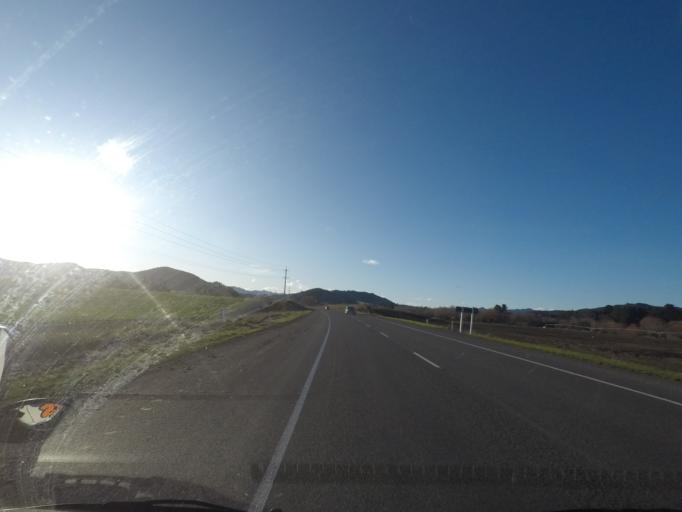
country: NZ
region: Canterbury
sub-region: Kaikoura District
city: Kaikoura
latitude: -42.6980
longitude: 173.3020
